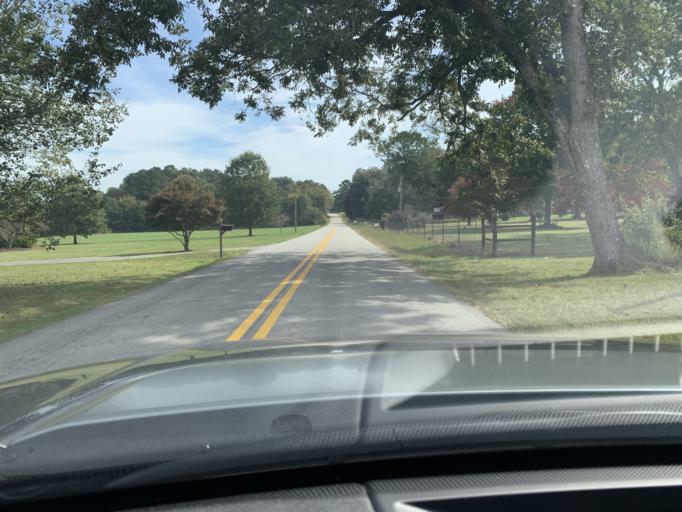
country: US
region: Georgia
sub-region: Polk County
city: Cedartown
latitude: 33.9715
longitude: -85.2641
